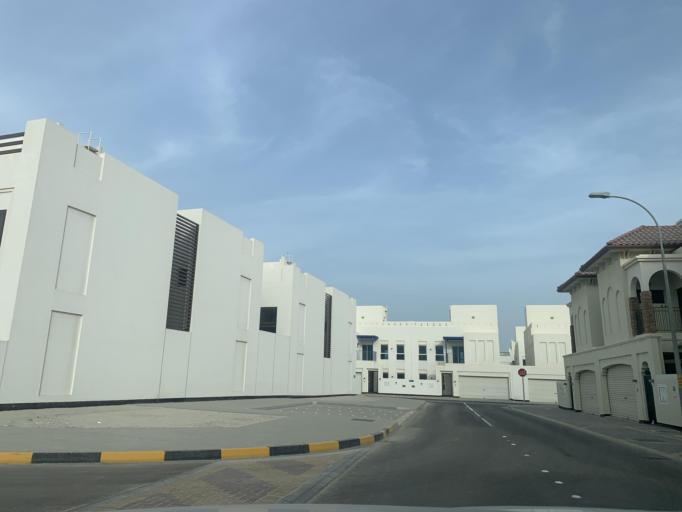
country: BH
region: Muharraq
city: Al Muharraq
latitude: 26.3146
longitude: 50.6199
